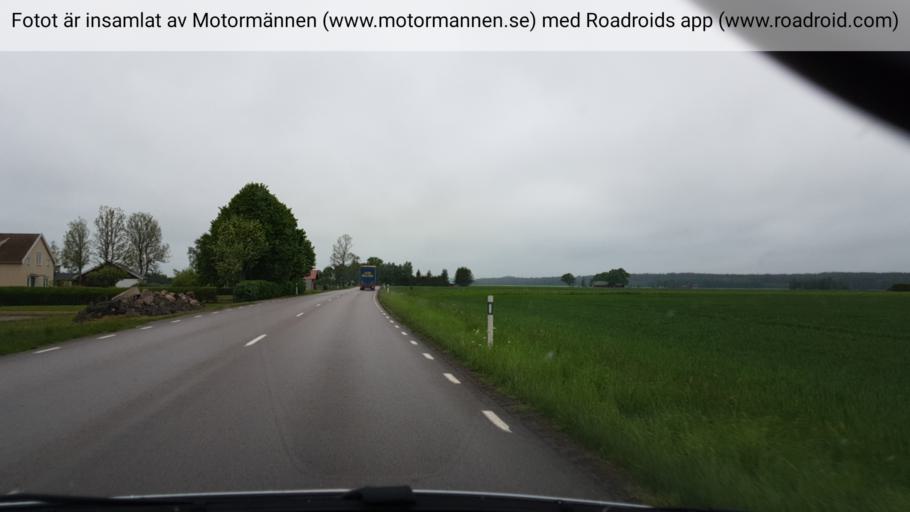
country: SE
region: Vaestra Goetaland
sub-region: Lidkopings Kommun
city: Lidkoping
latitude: 58.4254
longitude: 13.0405
